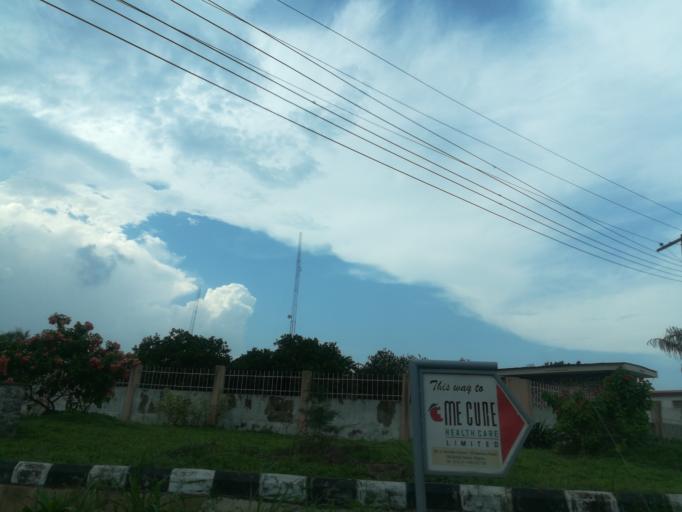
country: NG
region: Oyo
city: Ibadan
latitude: 7.4175
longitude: 3.9067
